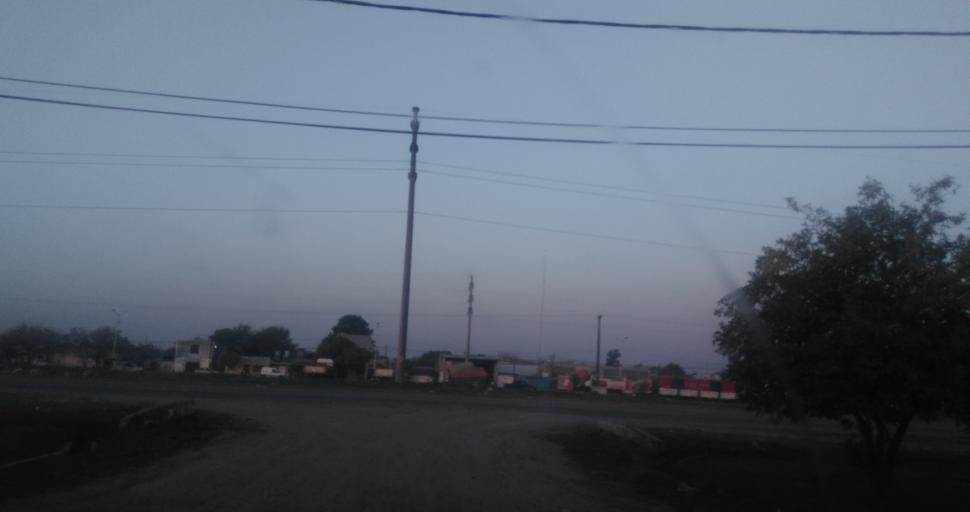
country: AR
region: Chaco
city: Resistencia
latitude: -27.4772
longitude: -59.0022
